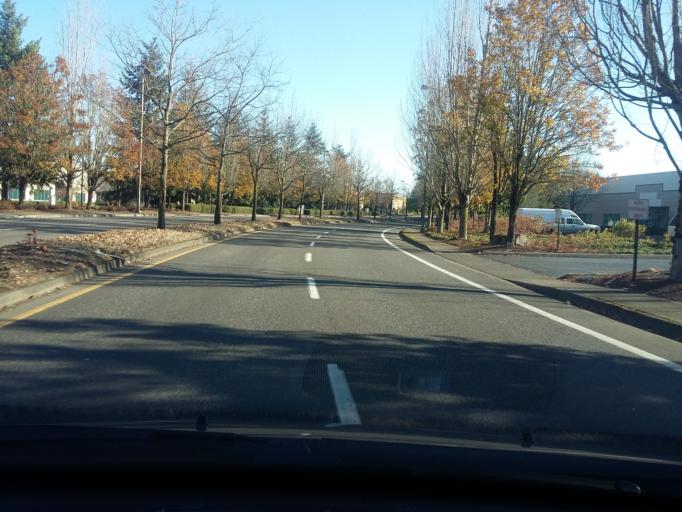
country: US
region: Washington
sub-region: Clark County
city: Mill Plain
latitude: 45.5619
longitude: -122.5199
